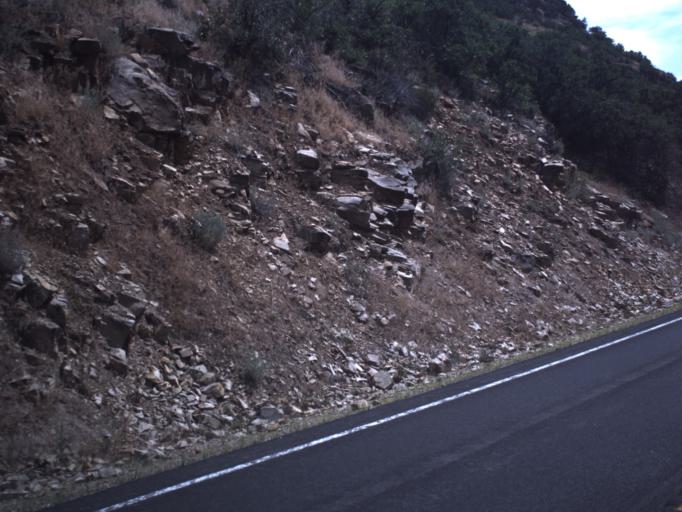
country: US
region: Utah
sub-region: Summit County
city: Francis
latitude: 40.5709
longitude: -111.2034
